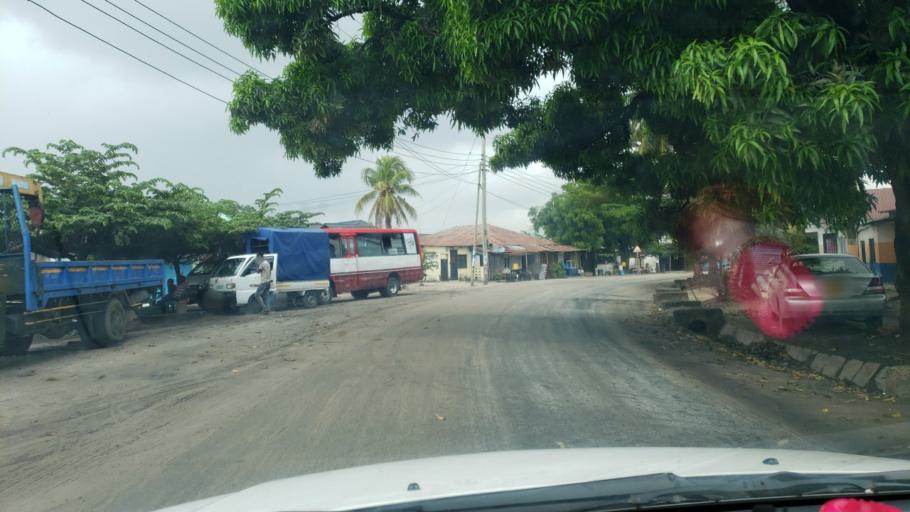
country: TZ
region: Dar es Salaam
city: Magomeni
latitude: -6.8084
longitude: 39.2495
